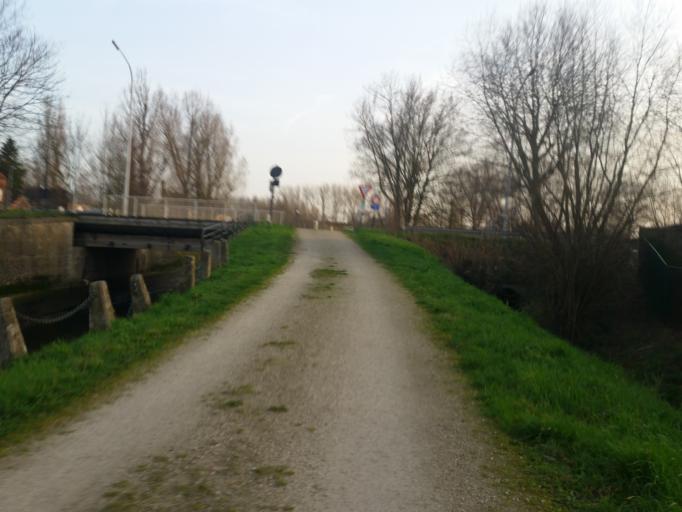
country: BE
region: Flanders
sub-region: Provincie Vlaams-Brabant
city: Zemst
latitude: 50.9874
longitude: 4.4699
